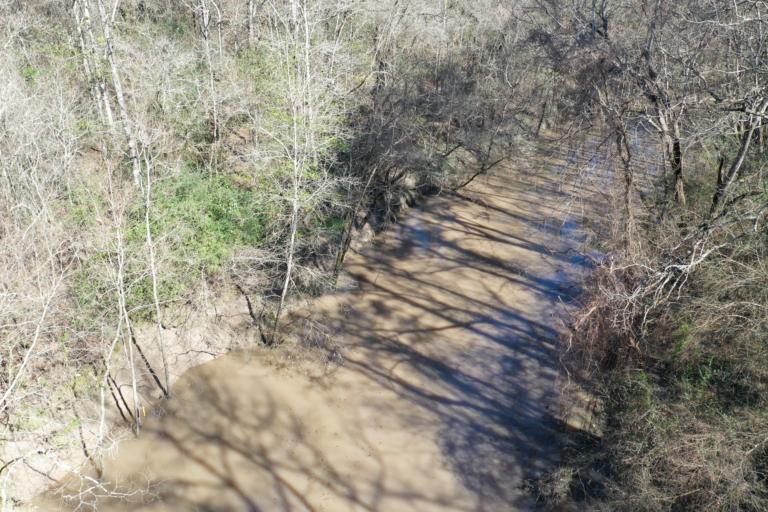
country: US
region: Louisiana
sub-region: Calcasieu Parish
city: Iowa
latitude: 30.3164
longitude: -93.0331
